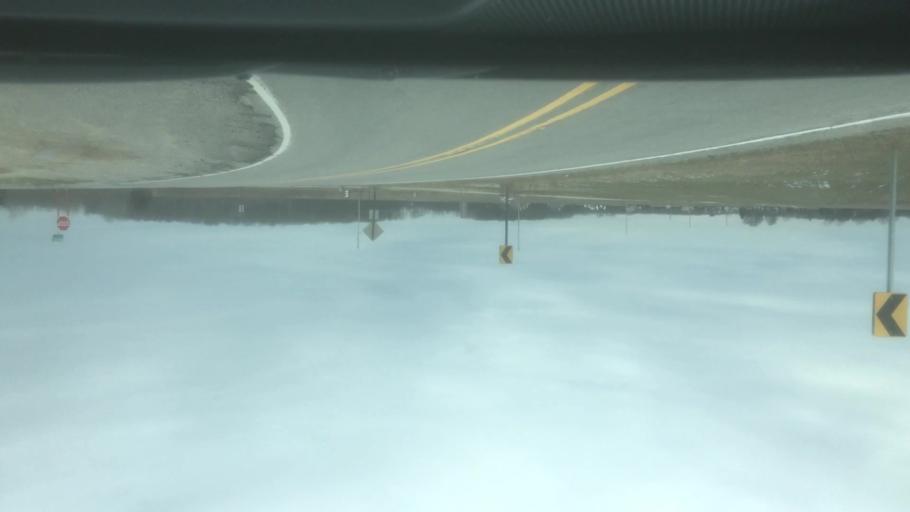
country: US
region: Michigan
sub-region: Bay County
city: Bay City
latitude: 43.6236
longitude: -83.9566
